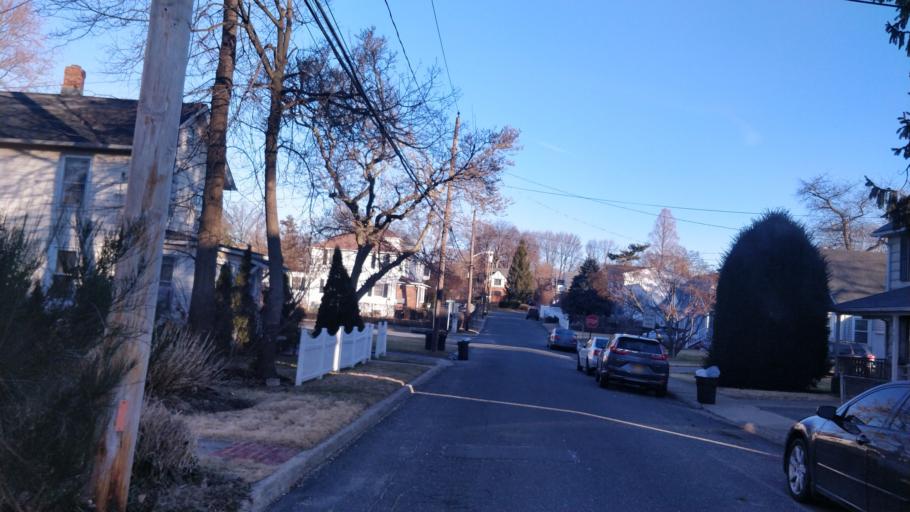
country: US
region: New York
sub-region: Nassau County
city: Glen Cove
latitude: 40.8692
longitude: -73.6411
